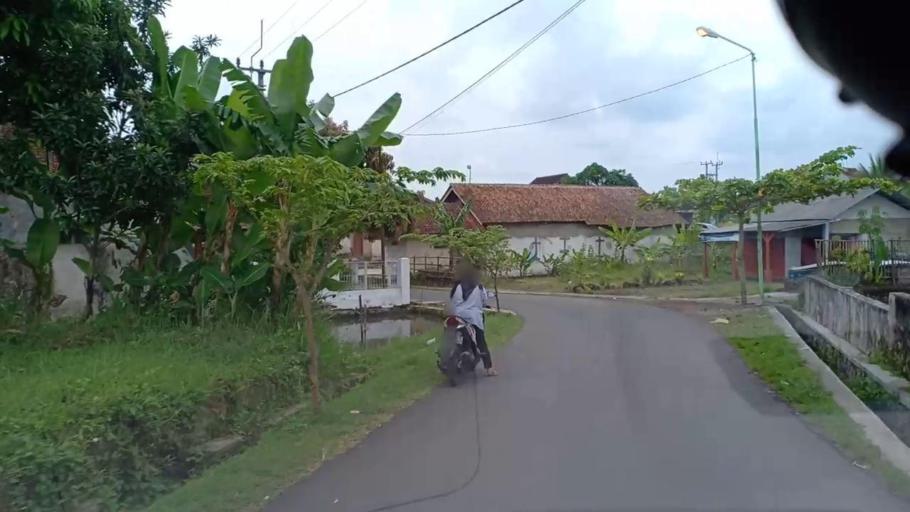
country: ID
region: West Java
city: Lemburwarung
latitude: -7.3376
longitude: 108.2711
